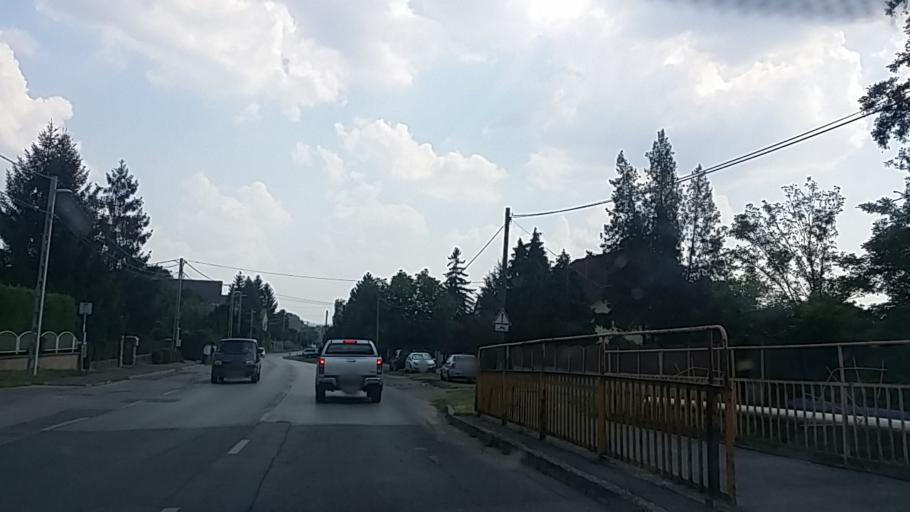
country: HU
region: Baranya
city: Pecs
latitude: 46.0726
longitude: 18.1864
